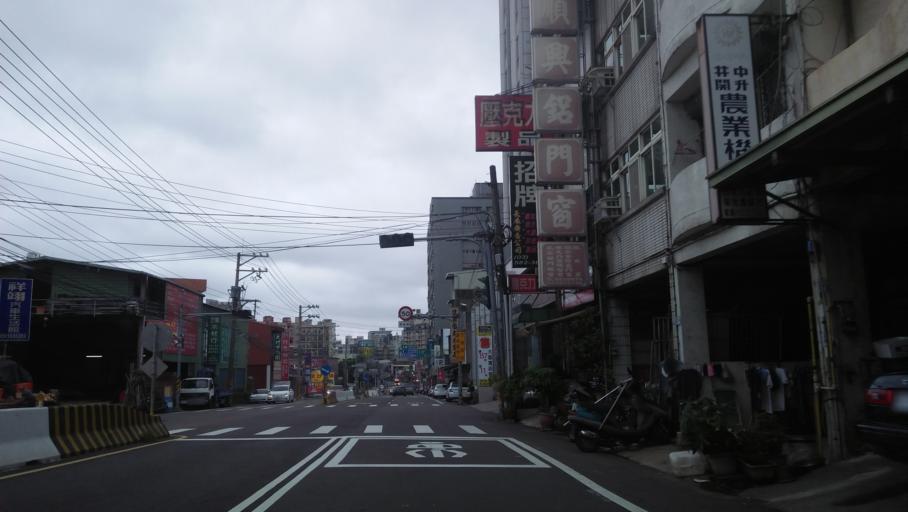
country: TW
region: Taiwan
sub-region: Hsinchu
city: Zhubei
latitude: 24.7795
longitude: 121.0296
